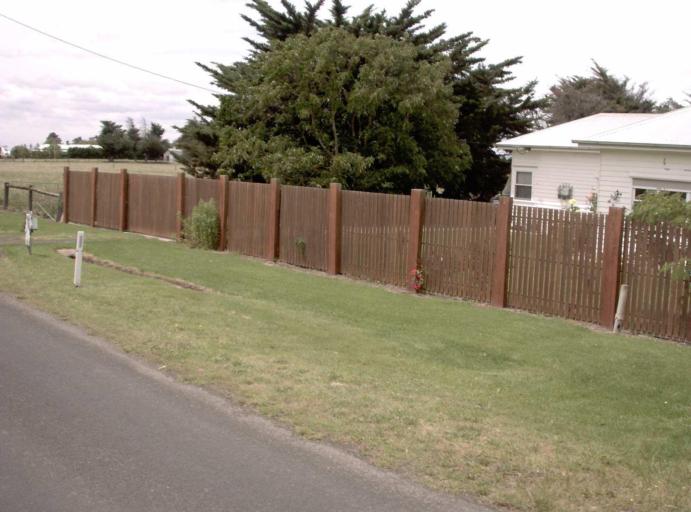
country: AU
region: Victoria
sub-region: Wellington
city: Sale
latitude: -38.1044
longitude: 147.1155
